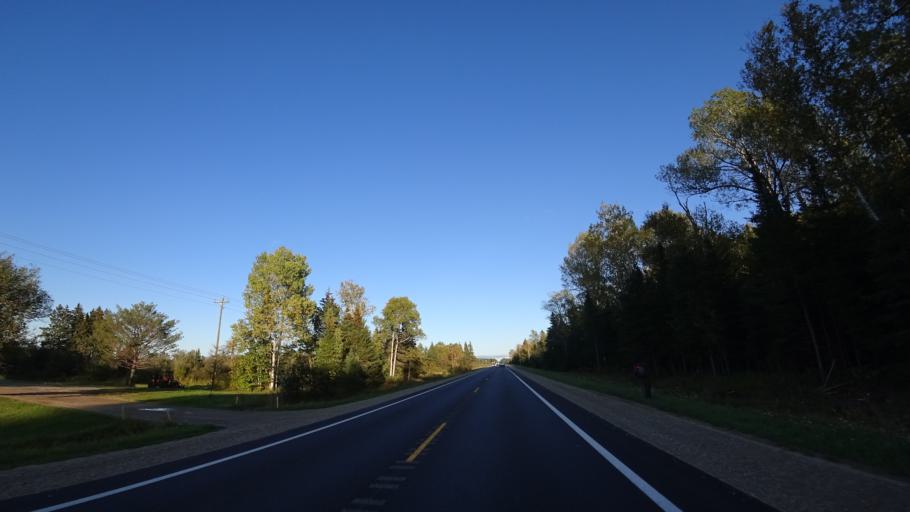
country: US
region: Michigan
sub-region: Luce County
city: Newberry
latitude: 46.3105
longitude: -85.5869
